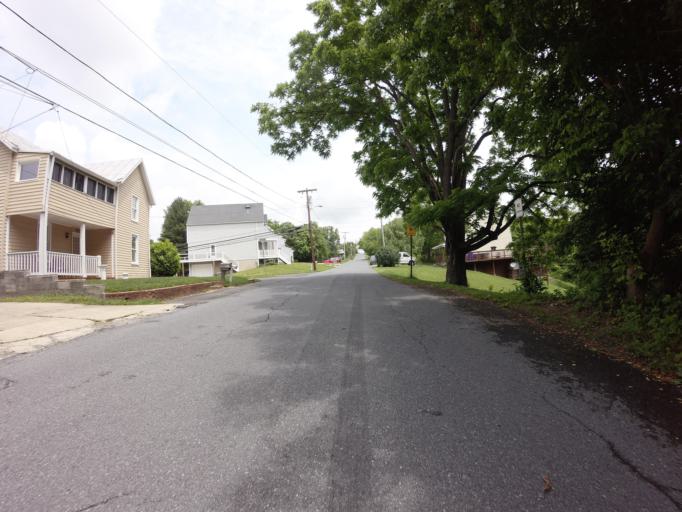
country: US
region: Maryland
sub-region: Frederick County
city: Brunswick
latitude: 39.3162
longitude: -77.6227
